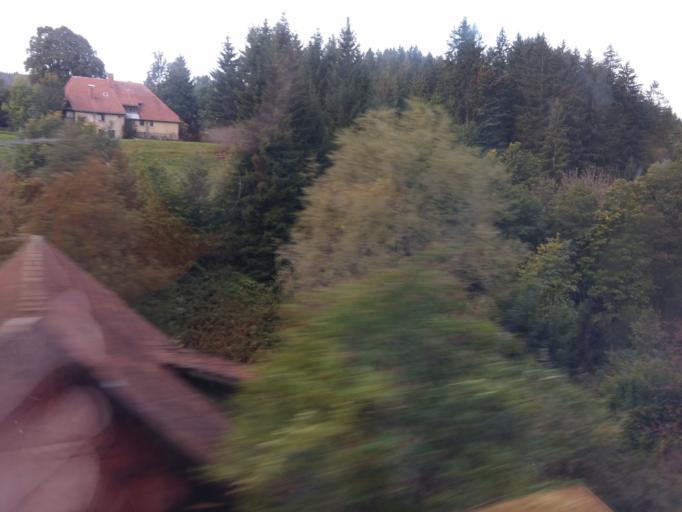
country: DE
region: Baden-Wuerttemberg
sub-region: Freiburg Region
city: Hinterzarten
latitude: 47.9100
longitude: 8.0966
